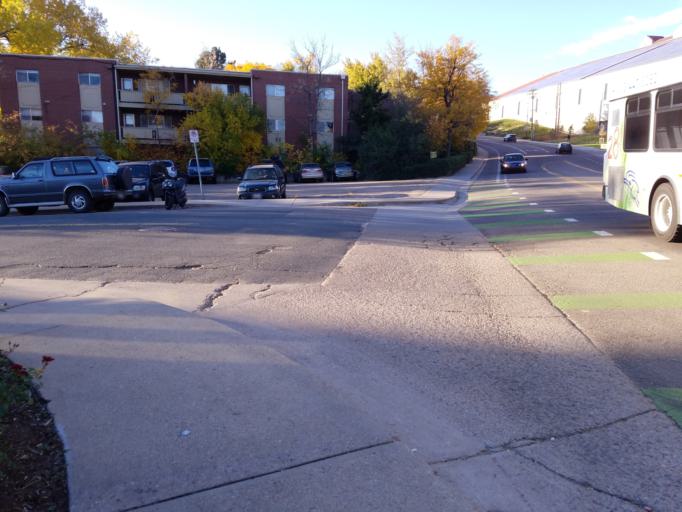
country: US
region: Colorado
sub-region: Boulder County
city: Boulder
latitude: 40.0110
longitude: -105.2634
